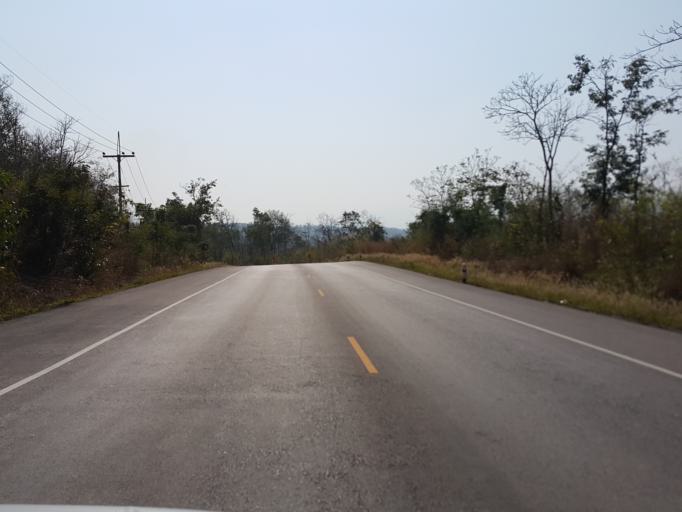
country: TH
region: Lampang
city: Mueang Pan
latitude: 18.8712
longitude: 99.5979
